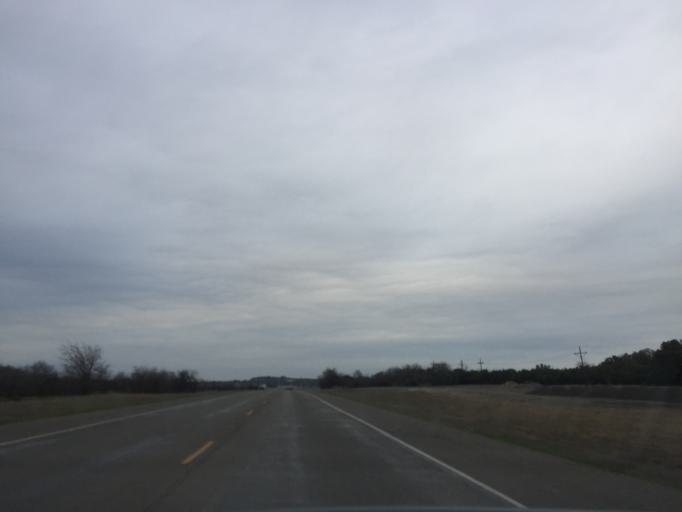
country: US
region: Texas
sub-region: Coryell County
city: Gatesville
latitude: 31.4602
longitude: -97.7167
